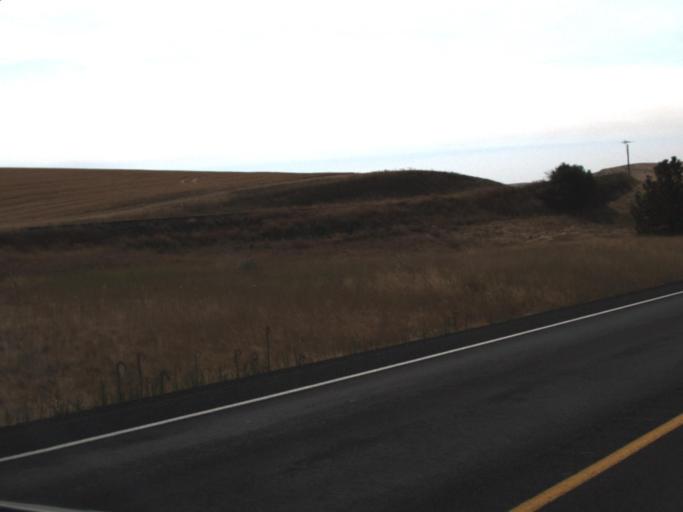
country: US
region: Washington
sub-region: Whitman County
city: Pullman
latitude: 46.8443
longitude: -117.1251
